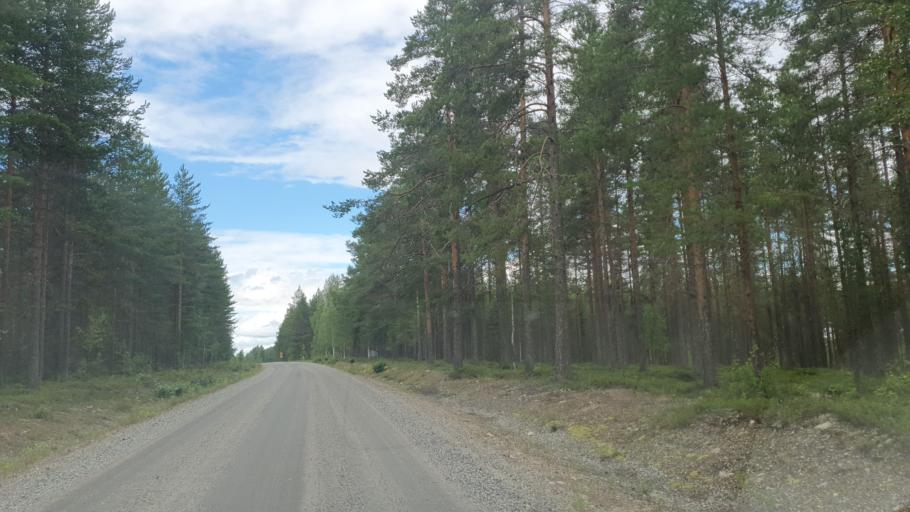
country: FI
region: Kainuu
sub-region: Kehys-Kainuu
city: Kuhmo
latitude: 64.1068
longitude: 29.3929
